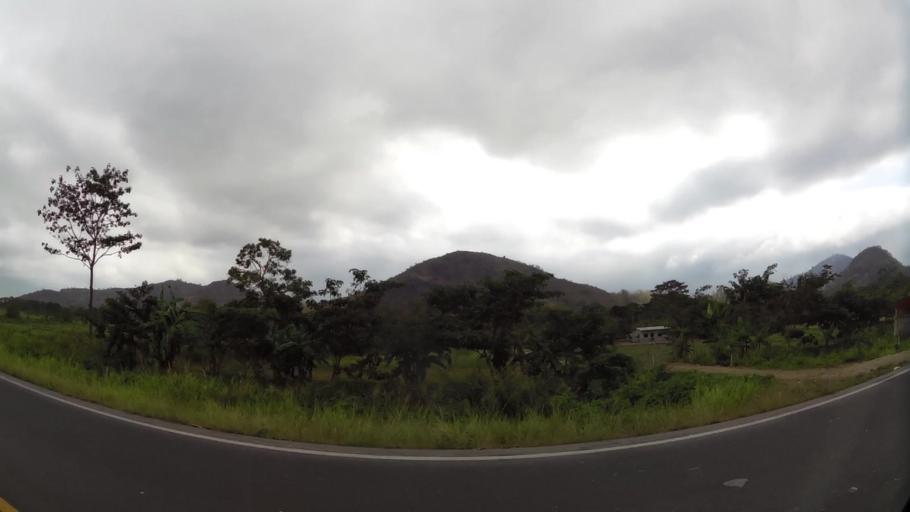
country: EC
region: Guayas
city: Coronel Marcelino Mariduena
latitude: -2.3919
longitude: -79.6305
